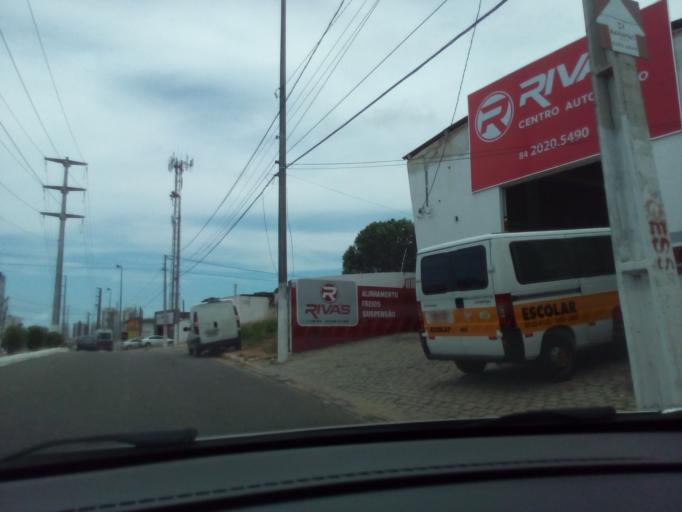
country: BR
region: Rio Grande do Norte
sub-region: Natal
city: Natal
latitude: -5.8465
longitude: -35.2155
